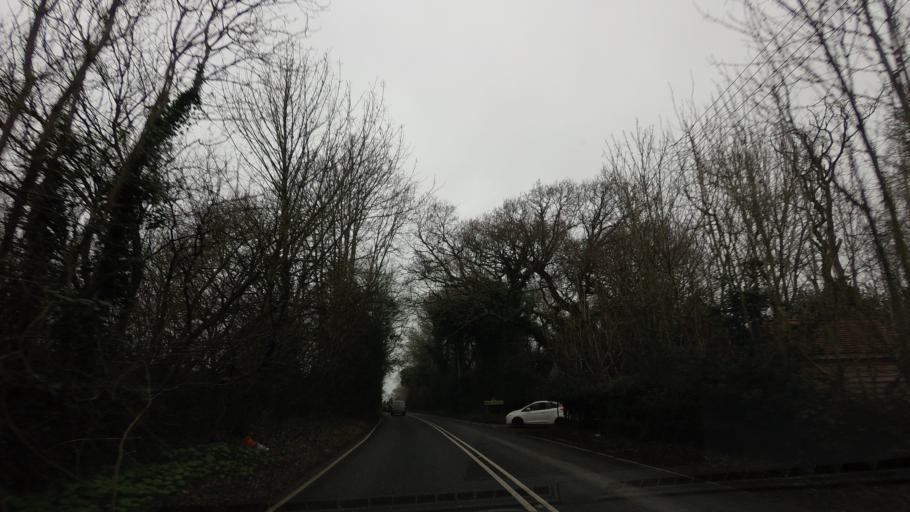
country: GB
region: England
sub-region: East Sussex
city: Battle
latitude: 50.9442
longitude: 0.5111
